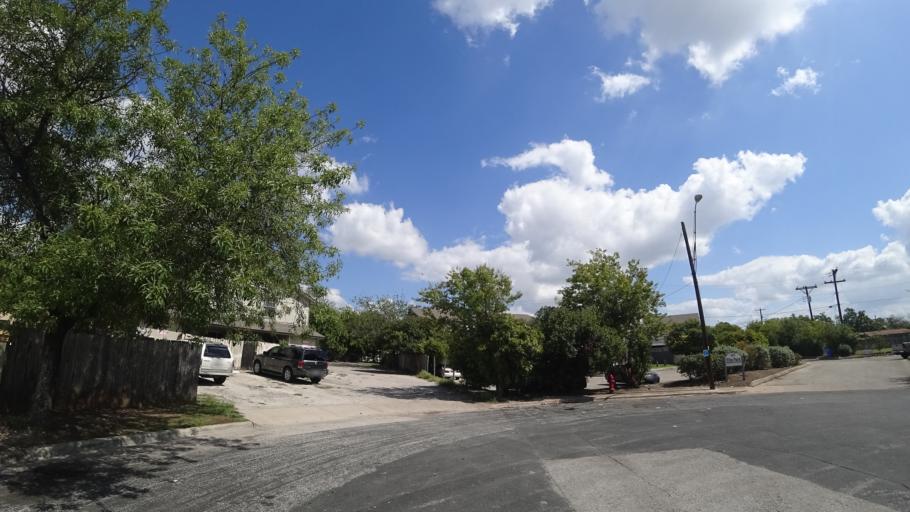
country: US
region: Texas
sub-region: Travis County
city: Wells Branch
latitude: 30.3679
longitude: -97.7231
